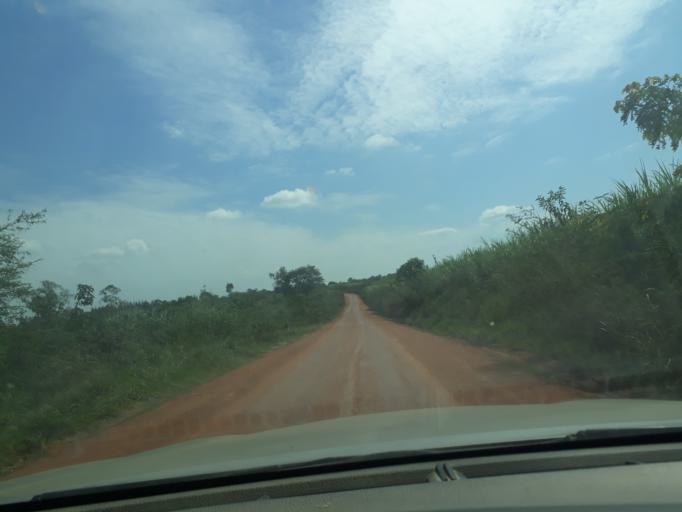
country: UG
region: Northern Region
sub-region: Zombo District
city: Paidha
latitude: 2.1475
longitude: 30.6355
